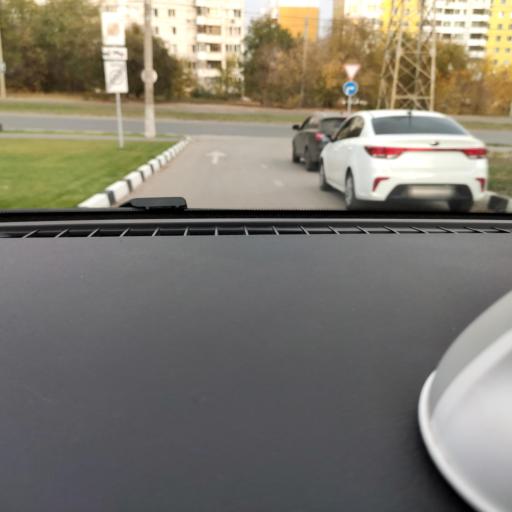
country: RU
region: Samara
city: Samara
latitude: 53.2100
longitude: 50.2125
